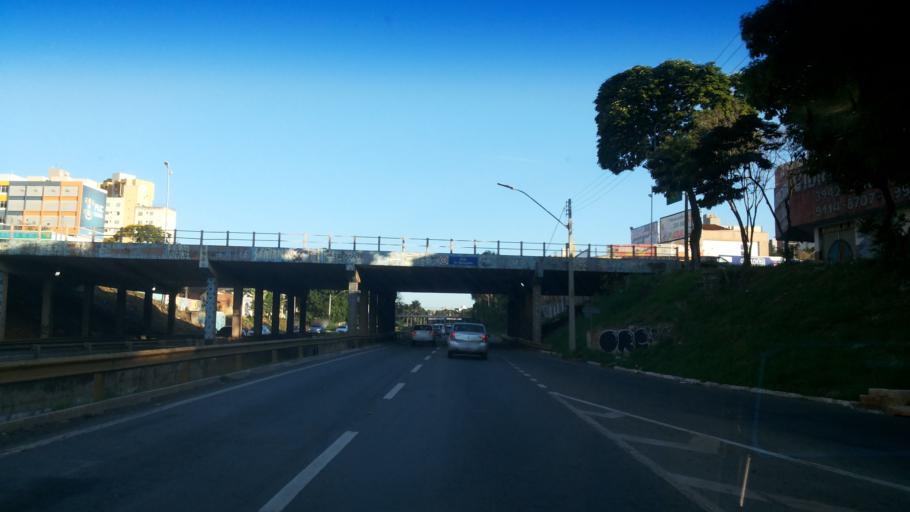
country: BR
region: Goias
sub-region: Goiania
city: Goiania
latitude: -16.6720
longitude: -49.2503
